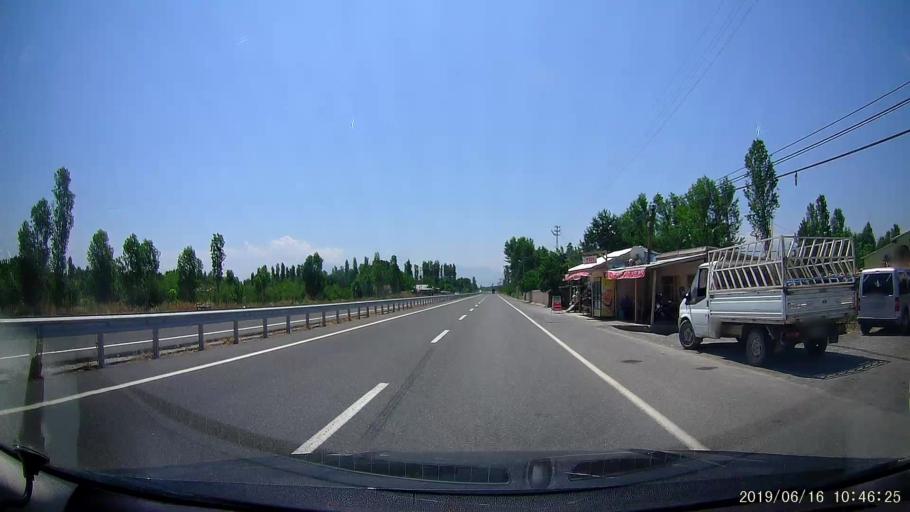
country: AM
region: Armavir
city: Shenavan
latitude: 40.0220
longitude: 43.8791
